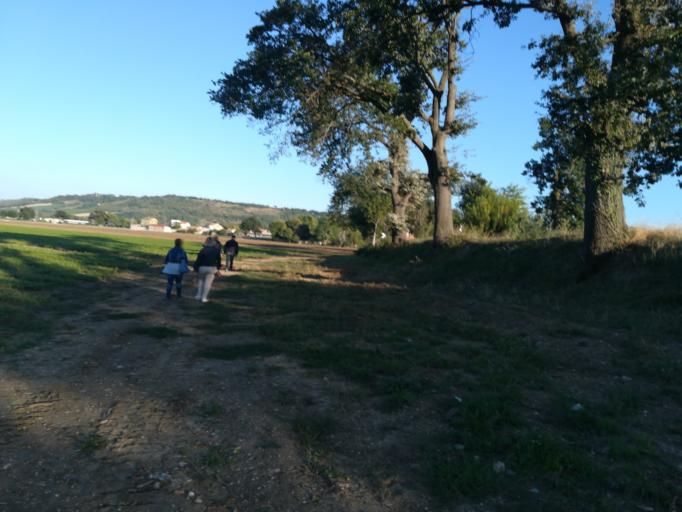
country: IT
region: The Marches
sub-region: Provincia di Macerata
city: Villa Potenza
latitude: 43.3300
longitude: 13.4172
